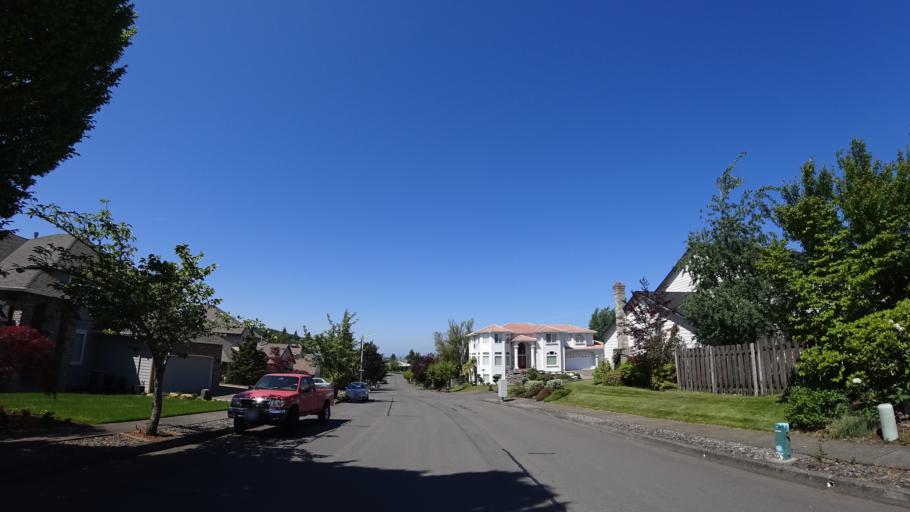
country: US
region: Oregon
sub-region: Multnomah County
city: Gresham
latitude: 45.4776
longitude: -122.4746
